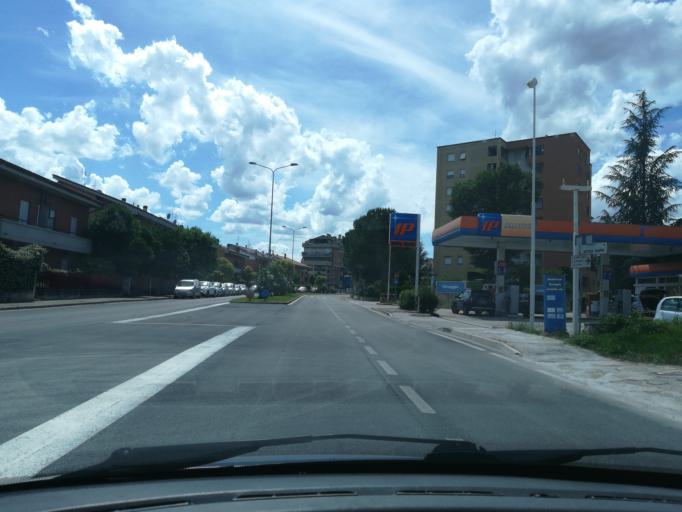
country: IT
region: The Marches
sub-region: Provincia di Macerata
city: Tolentino
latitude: 43.2139
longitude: 13.3005
